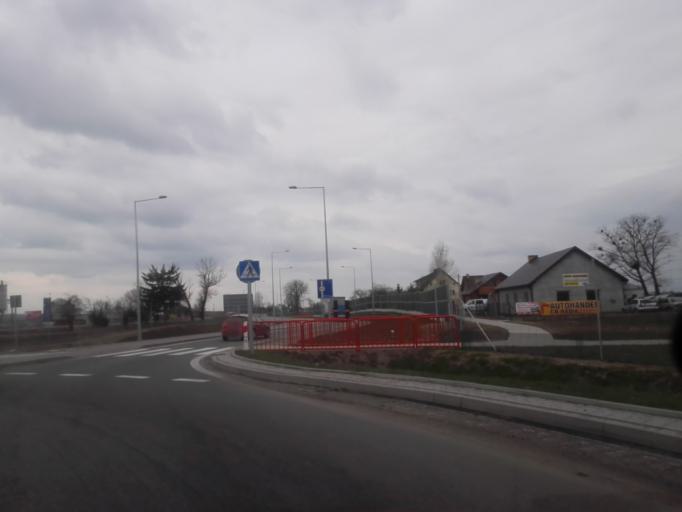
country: PL
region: Podlasie
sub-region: Powiat augustowski
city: Augustow
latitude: 53.8319
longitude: 22.9587
